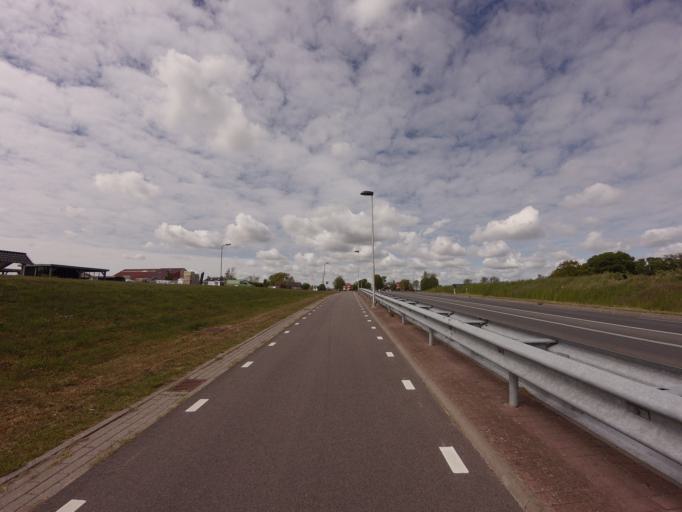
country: NL
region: Friesland
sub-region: Sudwest Fryslan
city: Woudsend
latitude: 52.9676
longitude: 5.6512
